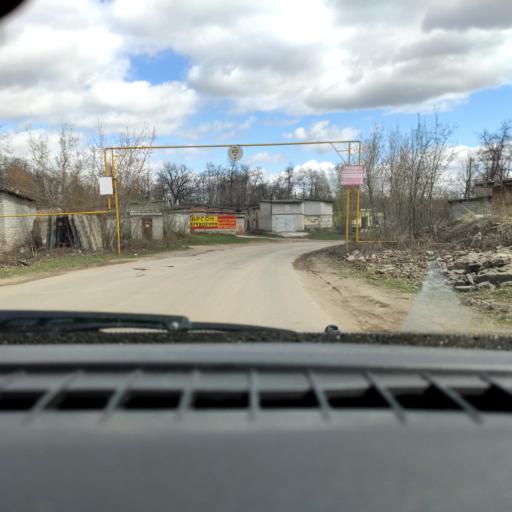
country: RU
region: Samara
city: Volzhskiy
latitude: 53.3542
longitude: 50.2069
